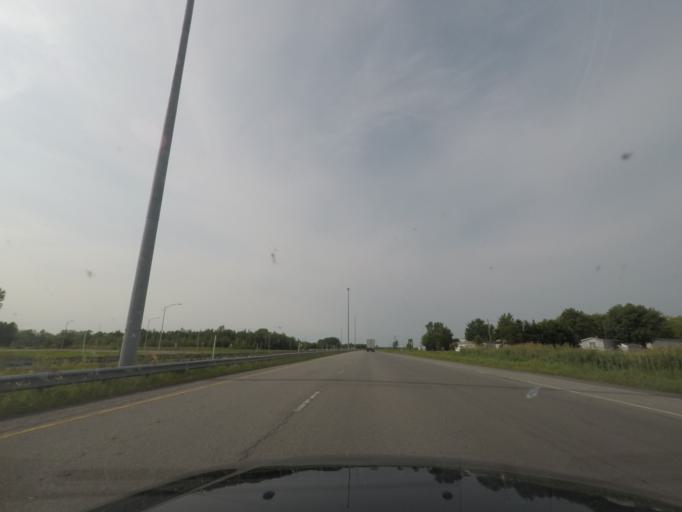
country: CA
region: Quebec
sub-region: Monteregie
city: Napierville
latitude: 45.1940
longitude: -73.4535
